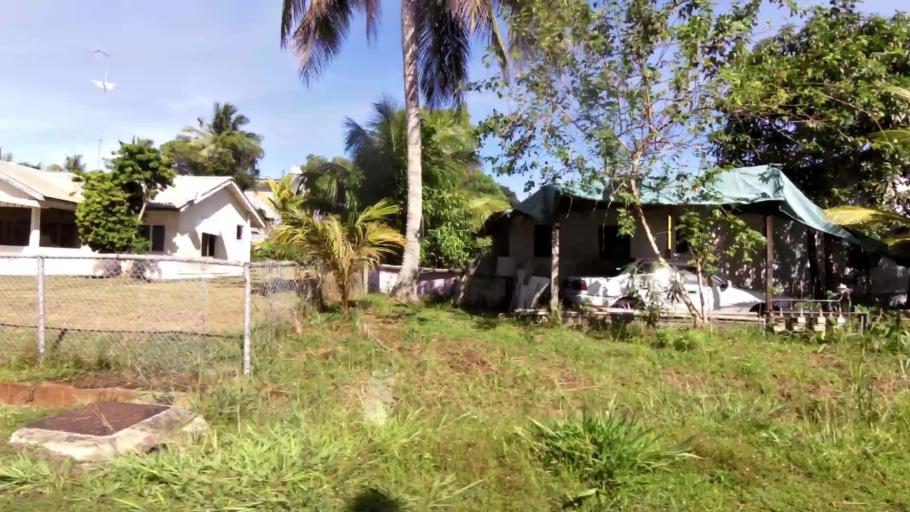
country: BN
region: Belait
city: Kuala Belait
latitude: 4.5809
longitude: 114.2023
